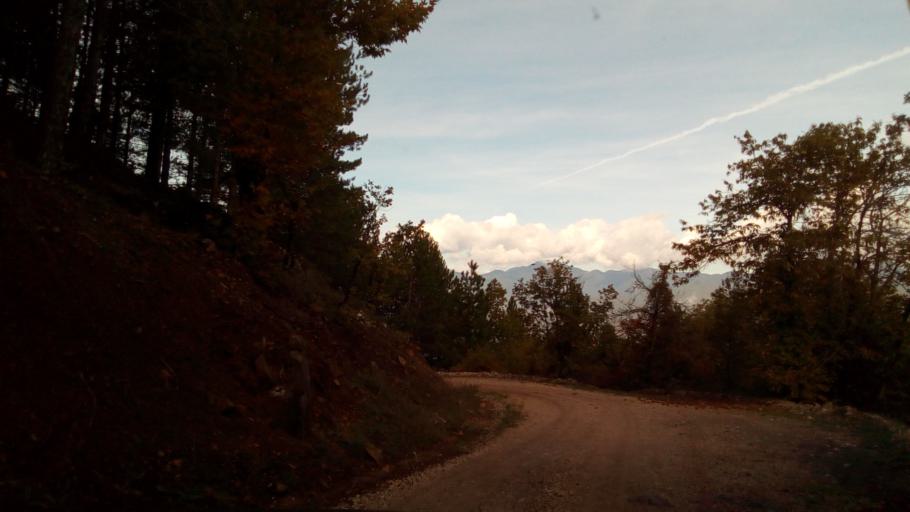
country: GR
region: West Greece
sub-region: Nomos Achaias
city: Kamarai
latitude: 38.4794
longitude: 22.0242
